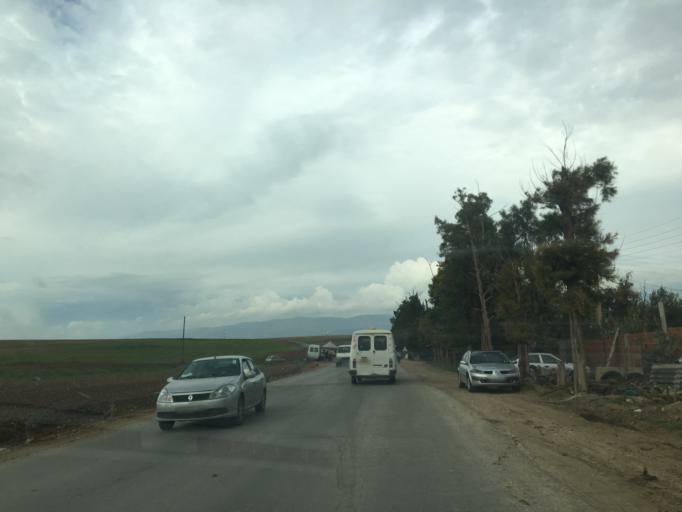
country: DZ
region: Bouira
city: Bouira
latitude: 36.3191
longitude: 3.8659
